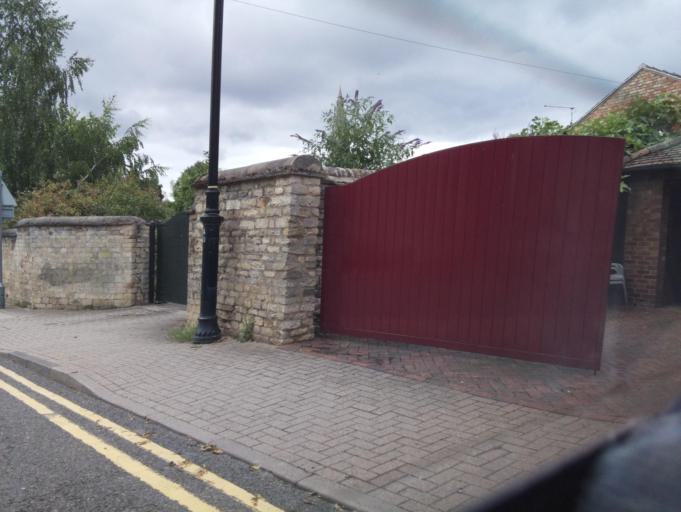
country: GB
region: England
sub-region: Lincolnshire
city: Stamford
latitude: 52.6509
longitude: -0.4757
